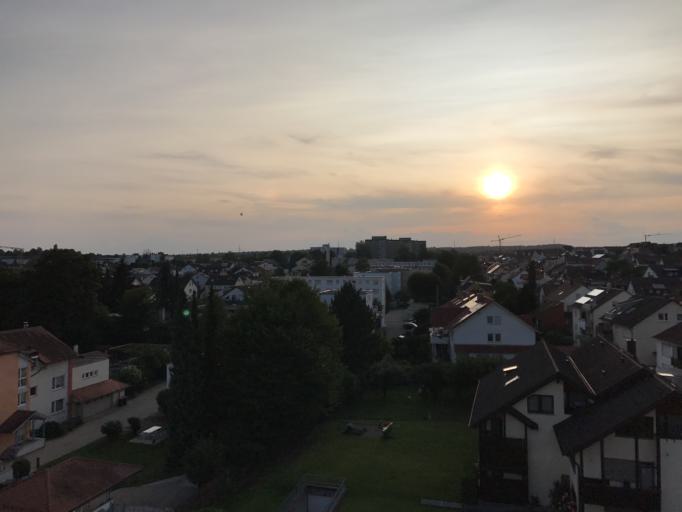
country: DE
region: Baden-Wuerttemberg
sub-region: Regierungsbezirk Stuttgart
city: Gartringen
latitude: 48.6397
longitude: 8.9045
